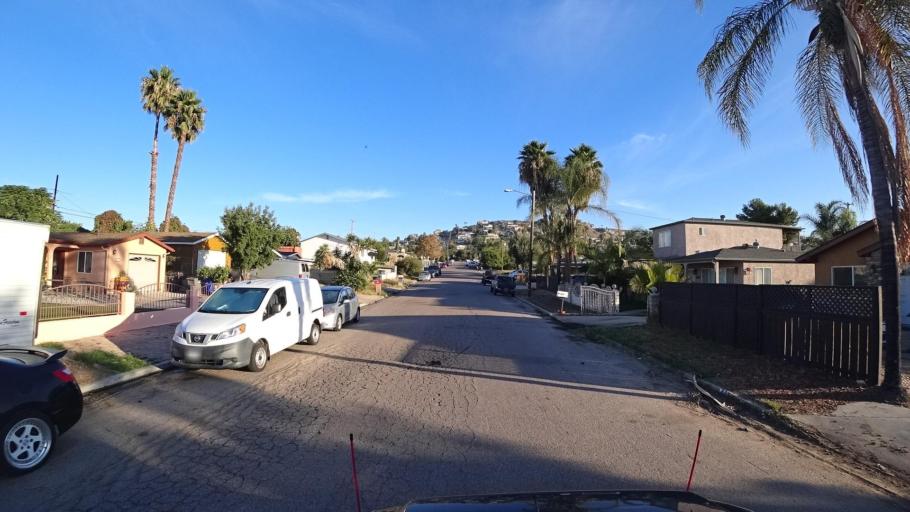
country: US
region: California
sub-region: San Diego County
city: La Presa
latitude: 32.7127
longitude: -116.9961
